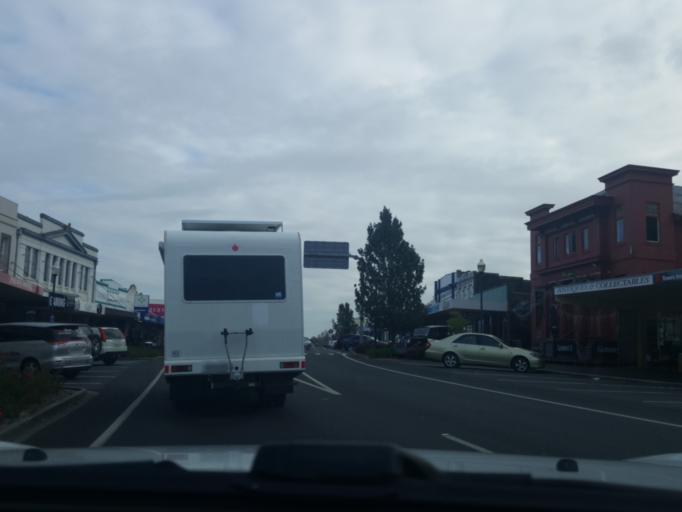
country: NZ
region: Waikato
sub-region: Hauraki District
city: Paeroa
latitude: -37.5431
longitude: 175.7122
